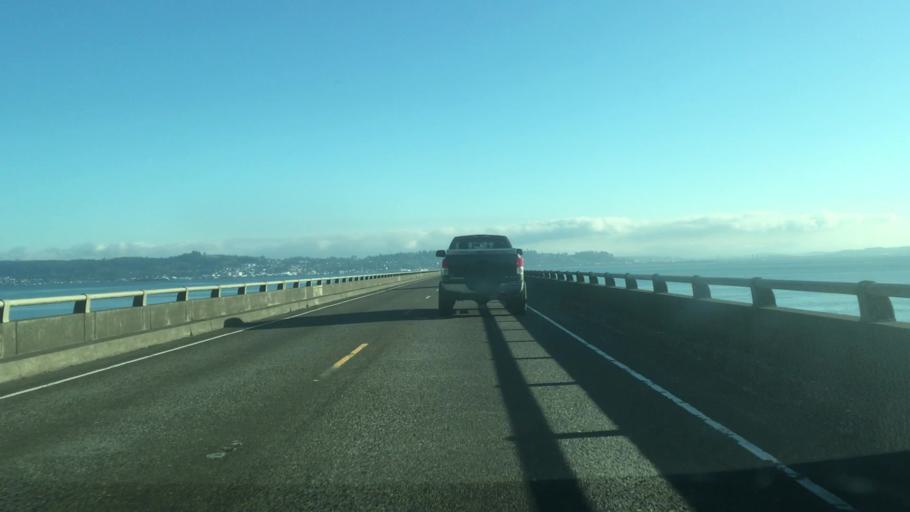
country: US
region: Oregon
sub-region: Clatsop County
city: Astoria
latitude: 46.2334
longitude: -123.8712
